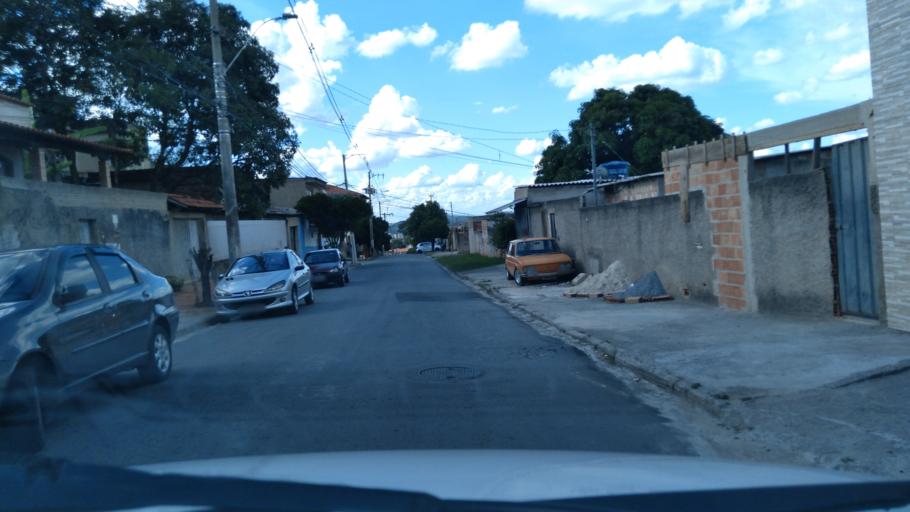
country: BR
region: Minas Gerais
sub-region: Belo Horizonte
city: Belo Horizonte
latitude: -19.8596
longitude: -43.8815
